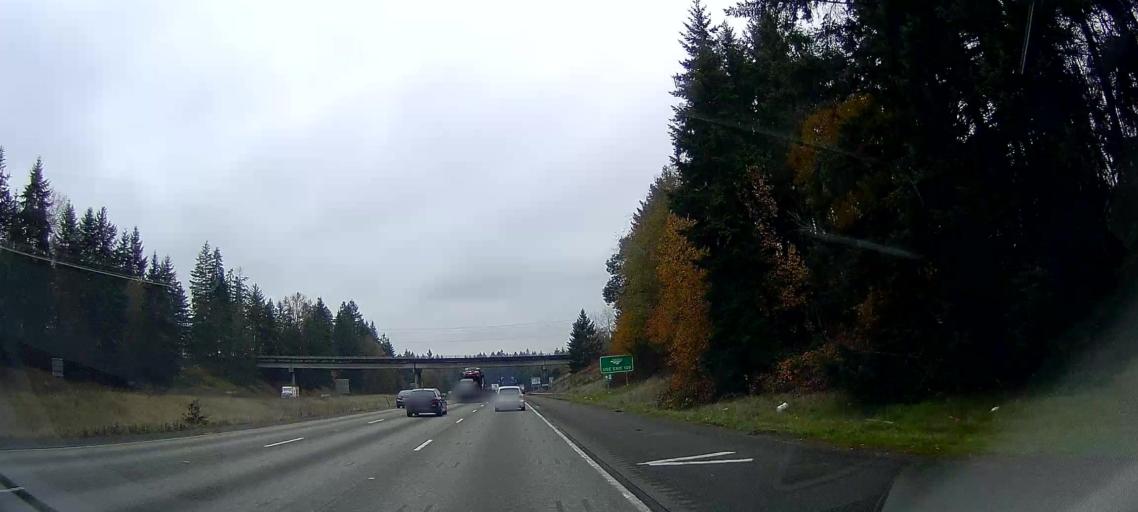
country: US
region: Washington
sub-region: Thurston County
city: Tanglewilde-Thompson Place
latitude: 47.0594
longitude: -122.7937
